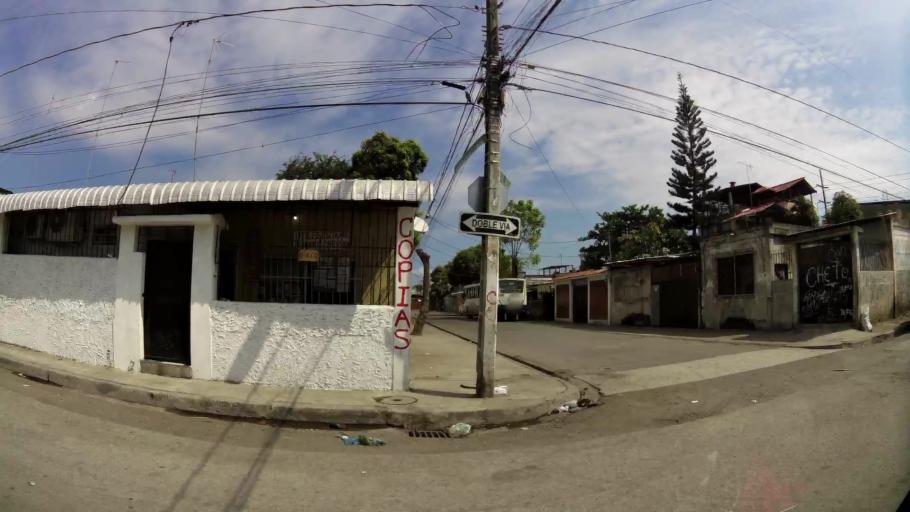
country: EC
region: Guayas
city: Guayaquil
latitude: -2.2603
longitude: -79.8851
